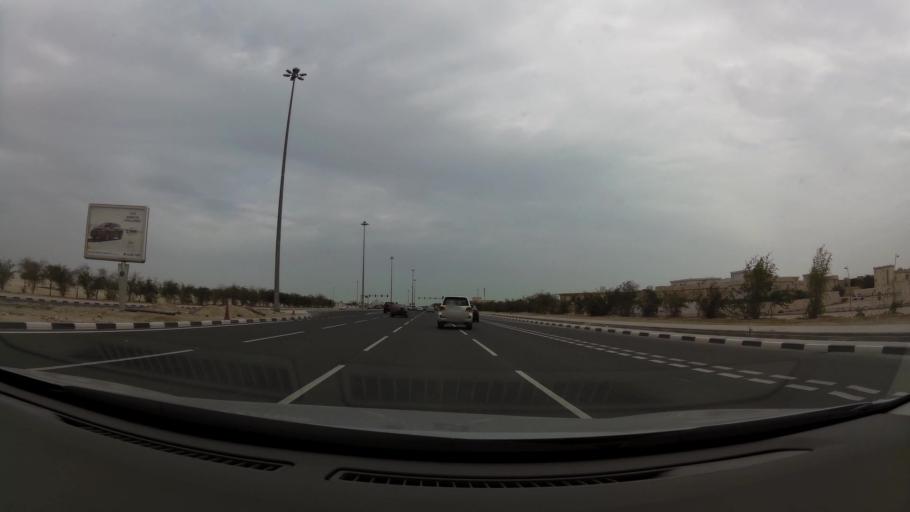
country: QA
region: Baladiyat ad Dawhah
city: Doha
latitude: 25.3484
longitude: 51.4863
